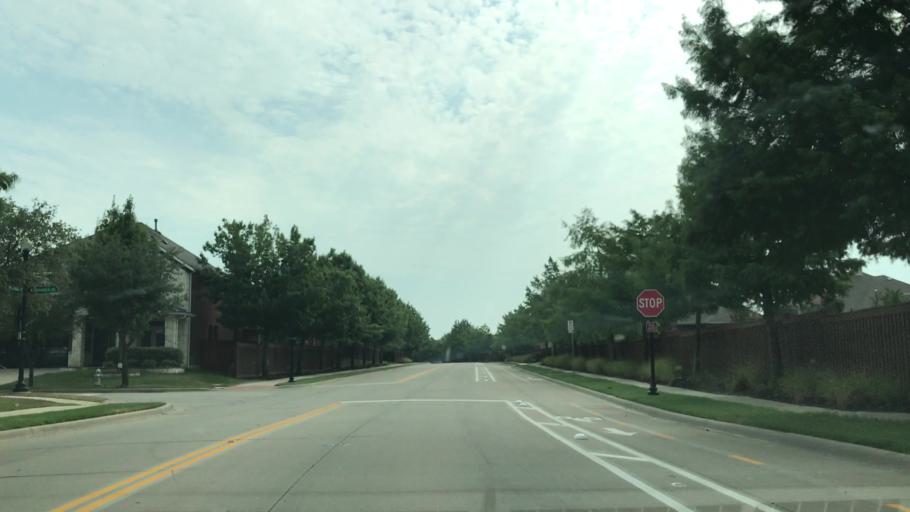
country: US
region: Texas
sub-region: Tarrant County
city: Keller
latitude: 32.9065
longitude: -97.2828
